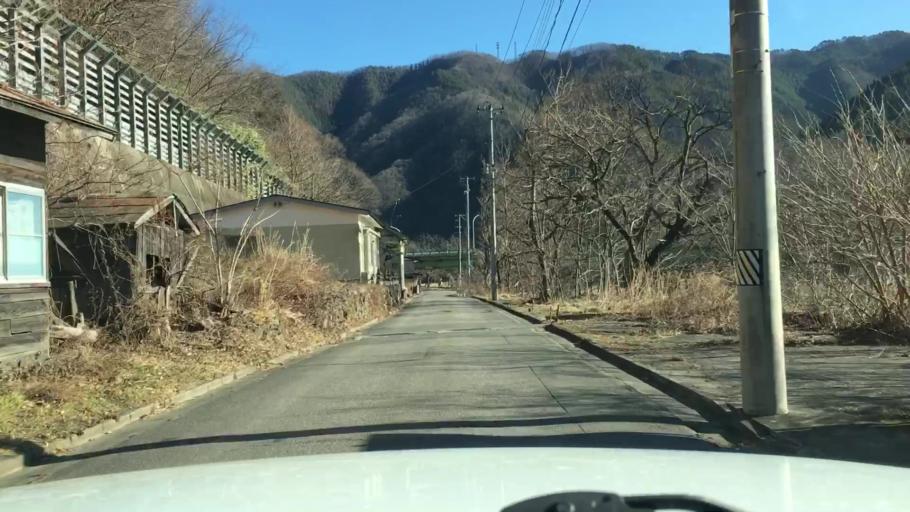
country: JP
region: Iwate
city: Miyako
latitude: 39.6215
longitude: 141.8015
